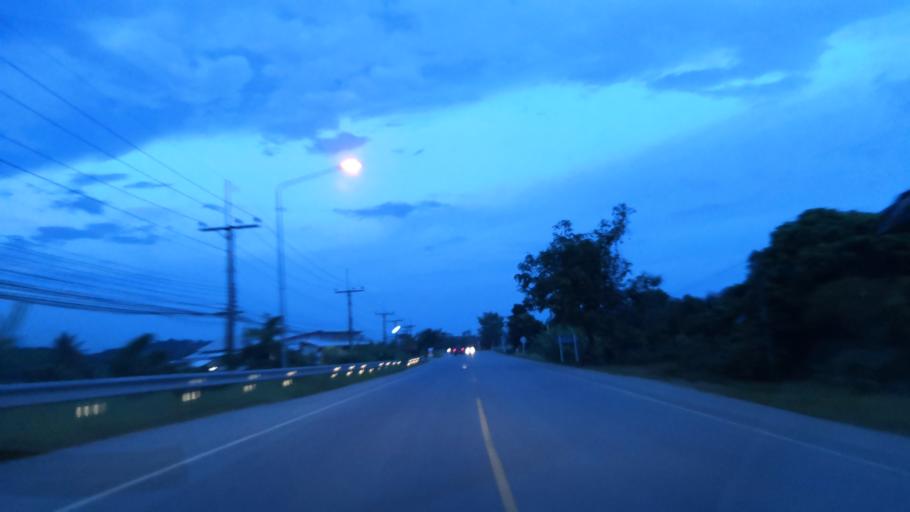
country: TH
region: Chiang Rai
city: Wiang Chiang Rung
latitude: 19.9873
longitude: 100.0273
